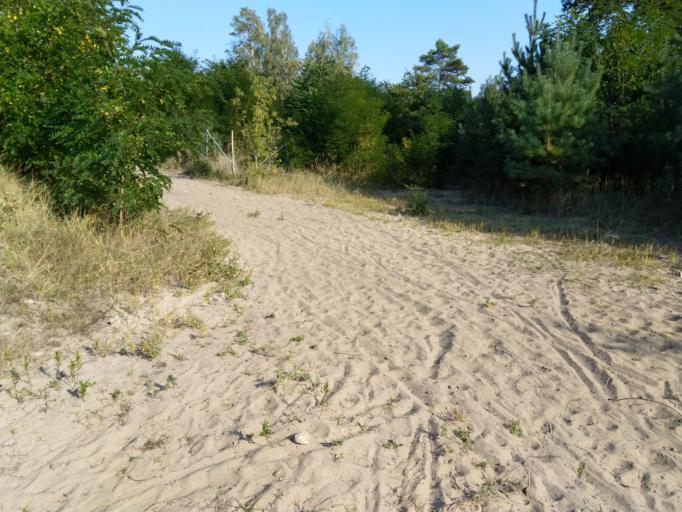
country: DE
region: Brandenburg
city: Erkner
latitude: 52.4424
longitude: 13.7345
